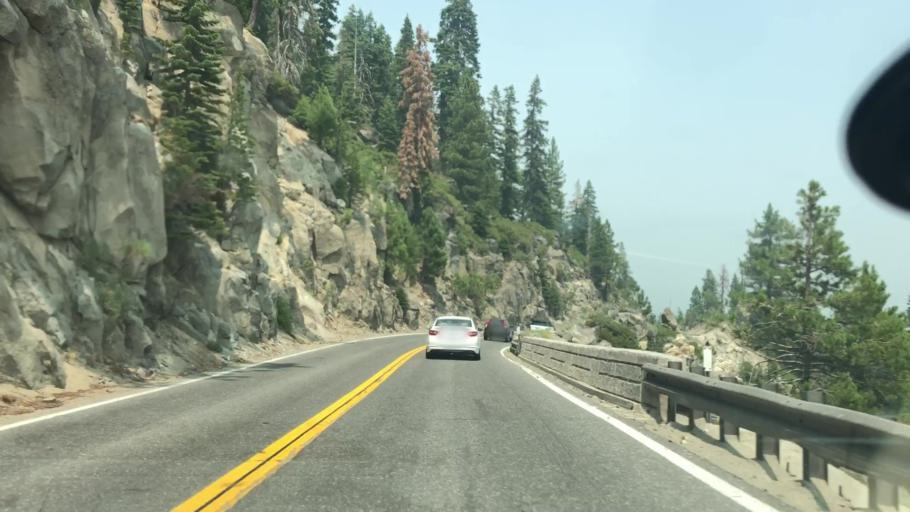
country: US
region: California
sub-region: El Dorado County
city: South Lake Tahoe
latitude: 38.8233
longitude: -120.0281
